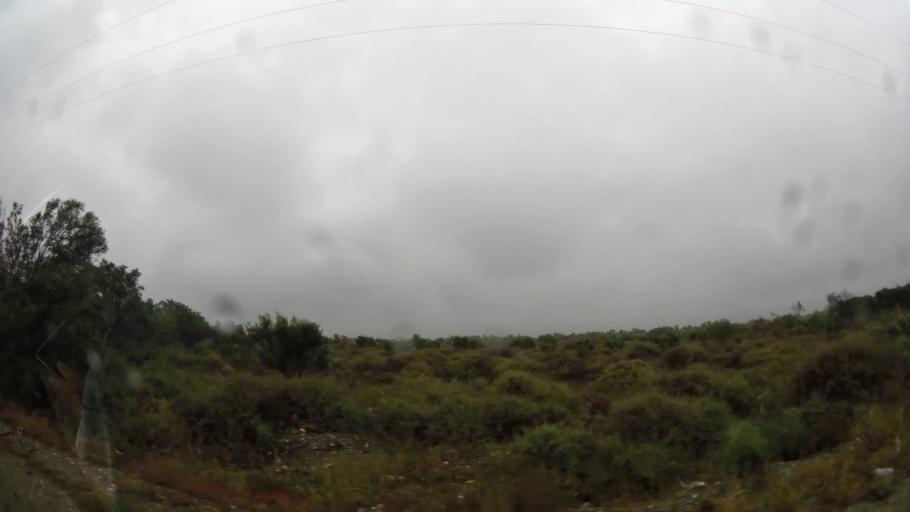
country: MA
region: Taza-Al Hoceima-Taounate
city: Imzourene
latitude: 35.1499
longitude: -3.8176
